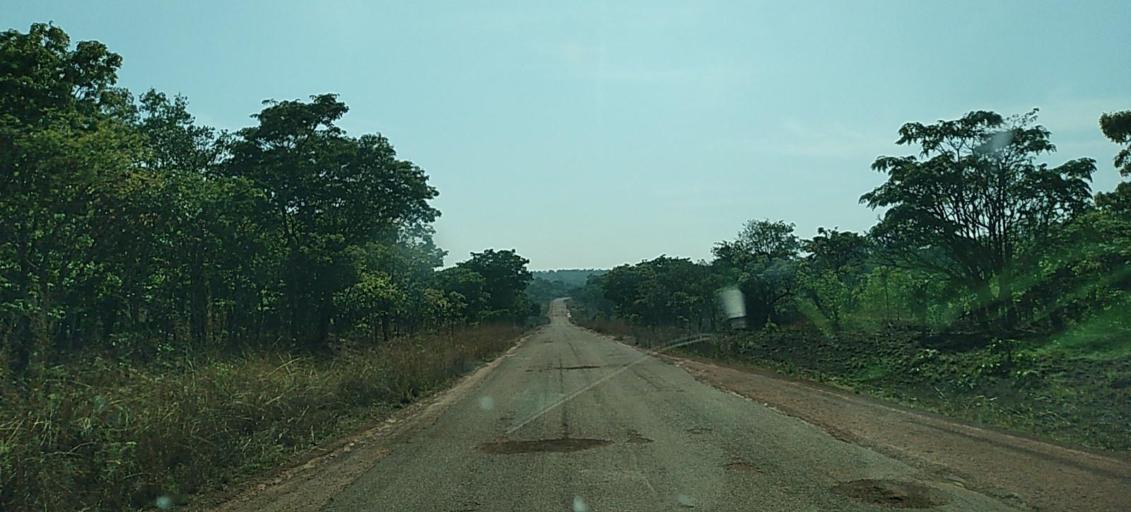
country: ZM
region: North-Western
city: Mwinilunga
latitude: -11.7856
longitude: 25.0361
